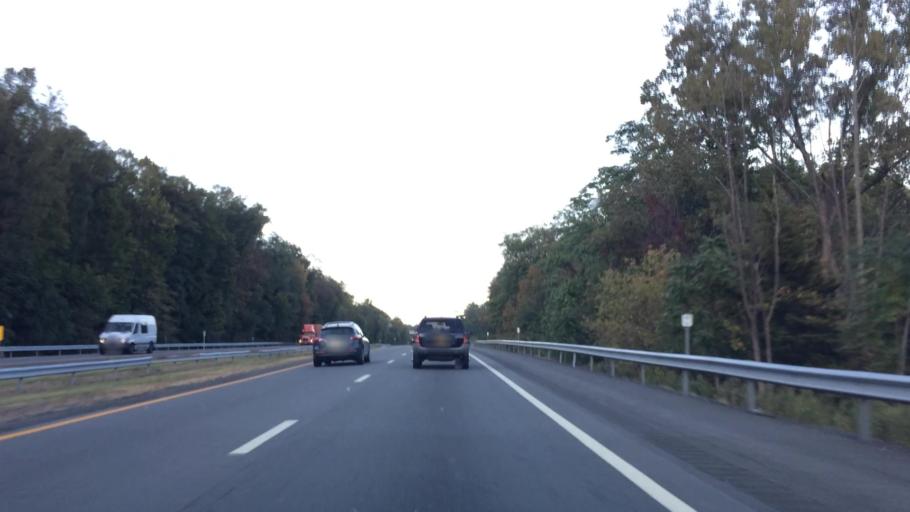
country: US
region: New York
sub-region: Orange County
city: Woodbury
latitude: 41.3854
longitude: -74.0997
